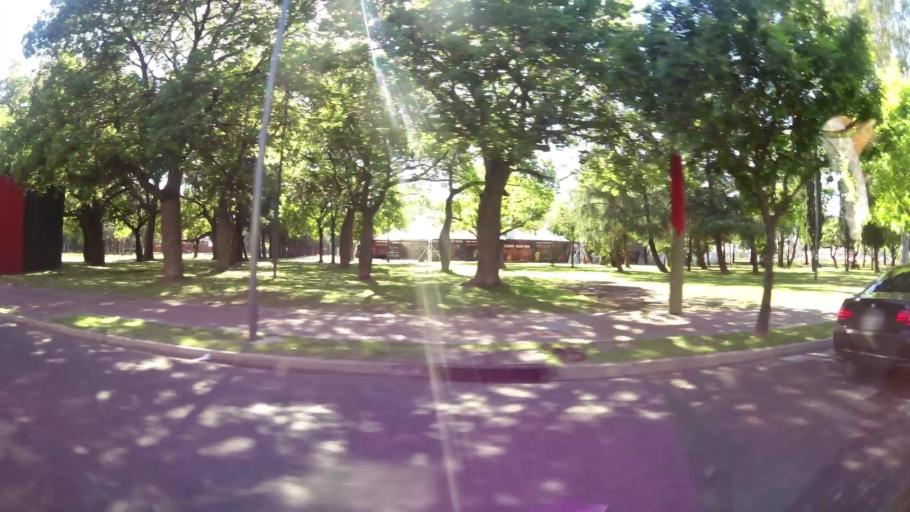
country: AR
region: Santa Fe
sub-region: Departamento de Rosario
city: Rosario
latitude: -32.9566
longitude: -60.6650
